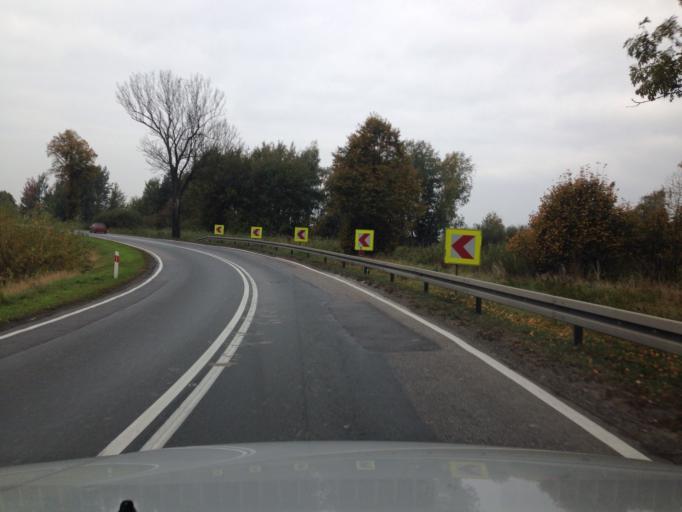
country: PL
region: Warmian-Masurian Voivodeship
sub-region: Powiat elblaski
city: Elblag
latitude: 54.1437
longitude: 19.3521
